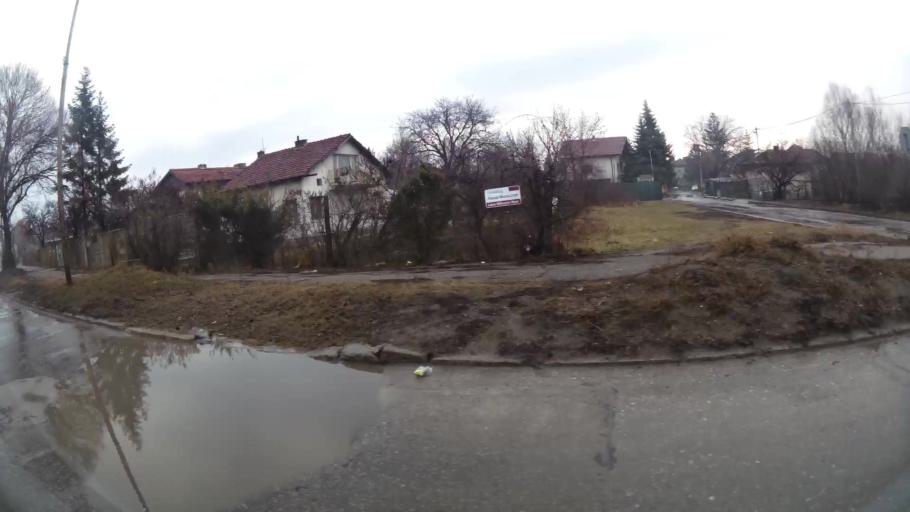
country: BG
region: Sofia-Capital
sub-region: Stolichna Obshtina
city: Sofia
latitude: 42.7354
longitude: 23.3432
